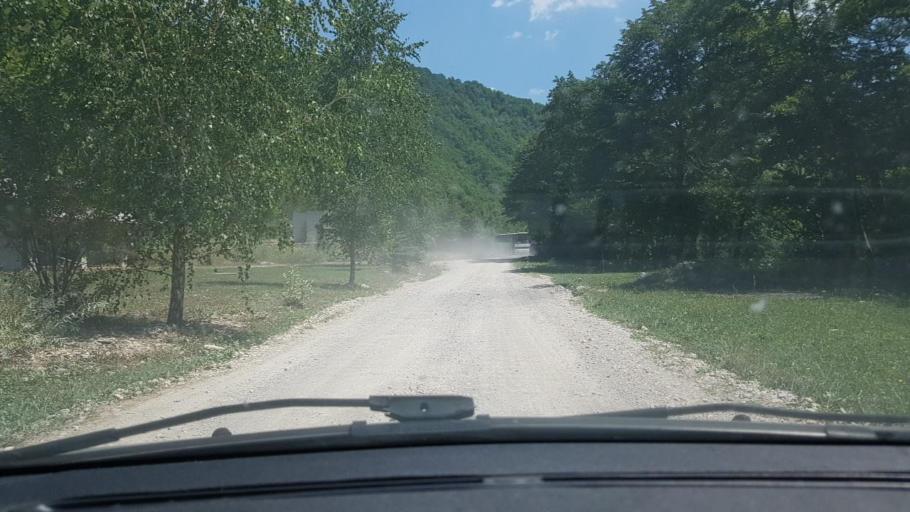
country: BA
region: Federation of Bosnia and Herzegovina
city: Orasac
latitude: 44.6563
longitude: 16.0253
